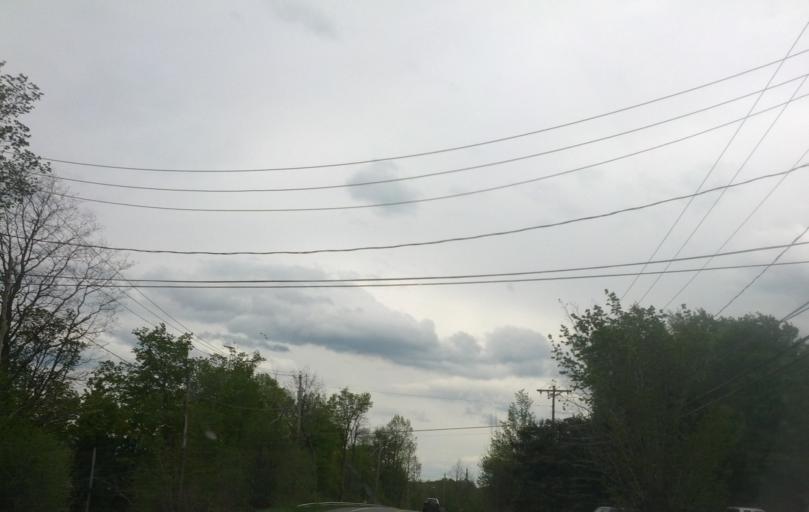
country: US
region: New York
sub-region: Onondaga County
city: Nedrow
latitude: 42.9917
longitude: -76.0905
